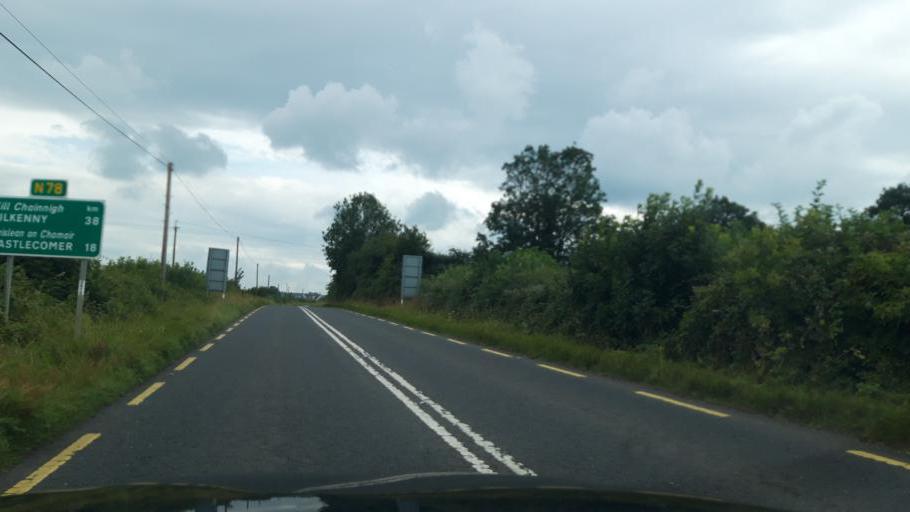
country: IE
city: Ballylinan
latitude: 52.9271
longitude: -7.0616
